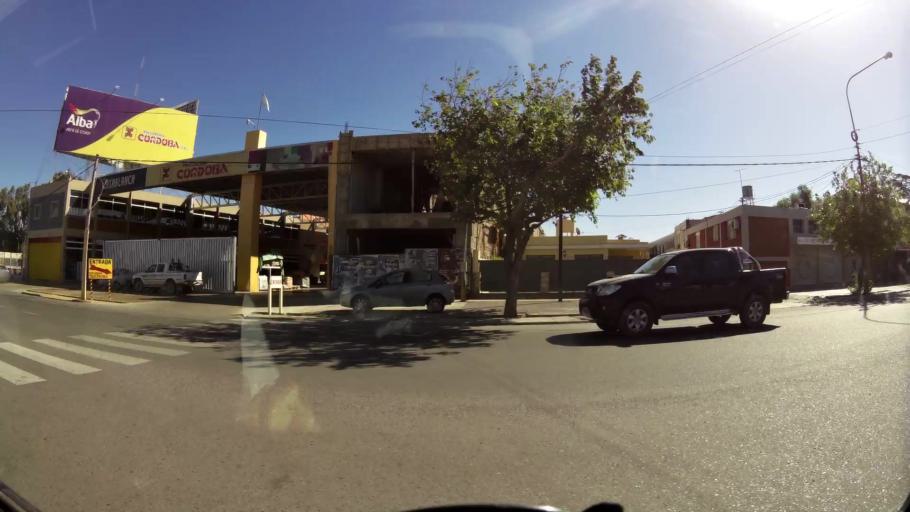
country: AR
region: San Juan
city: San Juan
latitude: -31.5470
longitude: -68.5334
